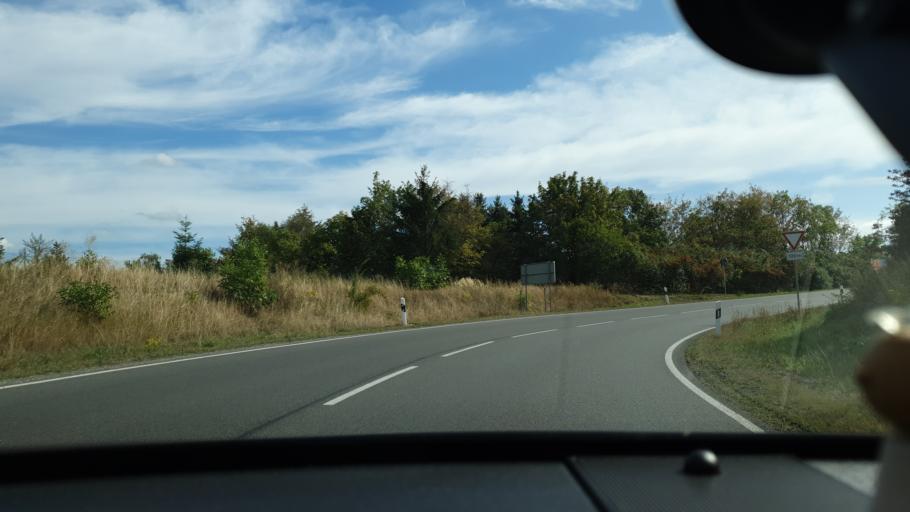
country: DE
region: Saxony
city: Eilenburg
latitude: 51.4593
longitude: 12.6124
